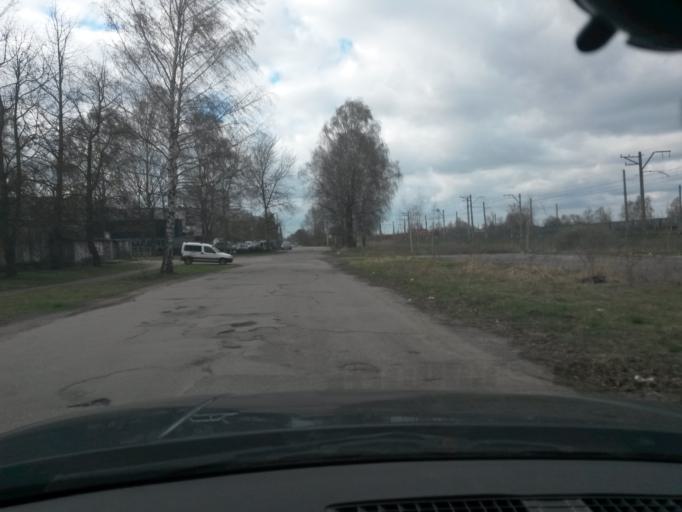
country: LV
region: Kekava
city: Kekava
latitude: 56.9000
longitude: 24.2193
